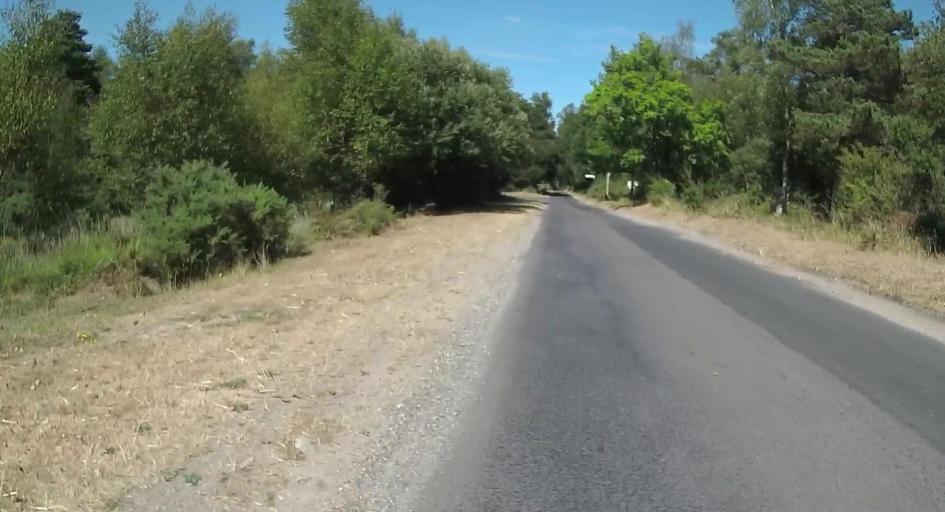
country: GB
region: England
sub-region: Dorset
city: Bovington Camp
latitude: 50.7245
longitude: -2.2538
